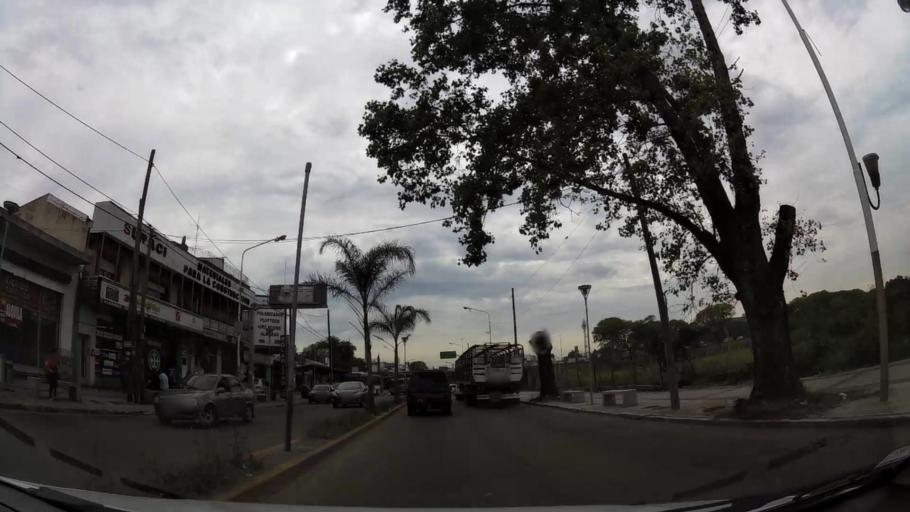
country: AR
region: Buenos Aires F.D.
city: Villa Lugano
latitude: -34.6753
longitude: -58.5039
